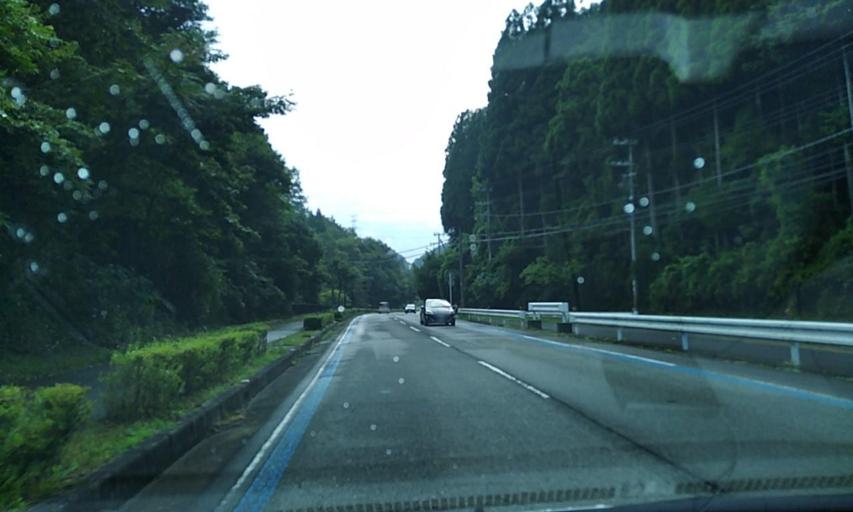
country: JP
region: Kyoto
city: Ayabe
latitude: 35.3220
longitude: 135.3219
